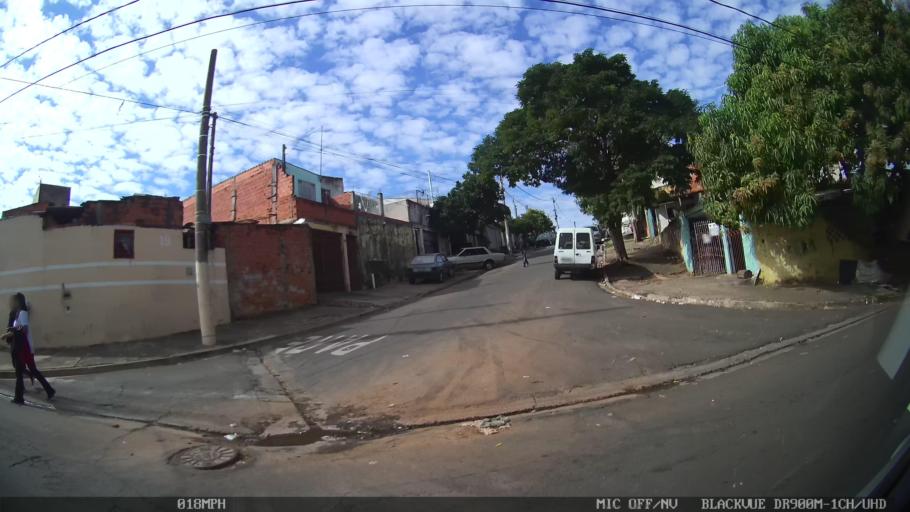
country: BR
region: Sao Paulo
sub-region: Santa Barbara D'Oeste
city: Santa Barbara d'Oeste
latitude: -22.7748
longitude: -47.3937
